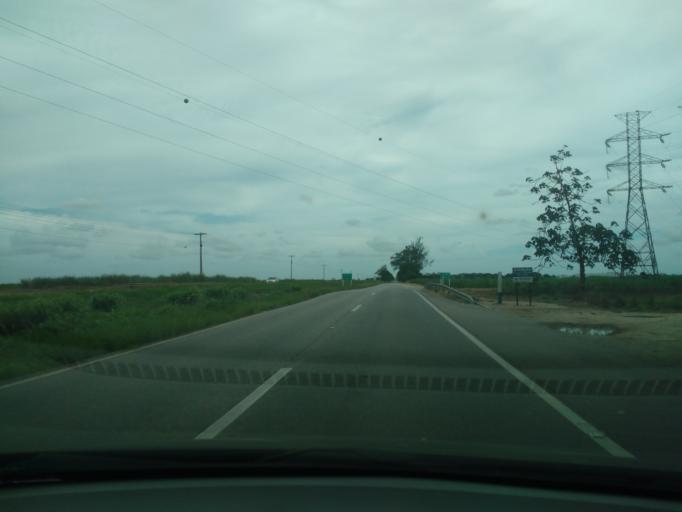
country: BR
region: Alagoas
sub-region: Rio Largo
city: Rio Largo
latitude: -9.4540
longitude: -35.8303
